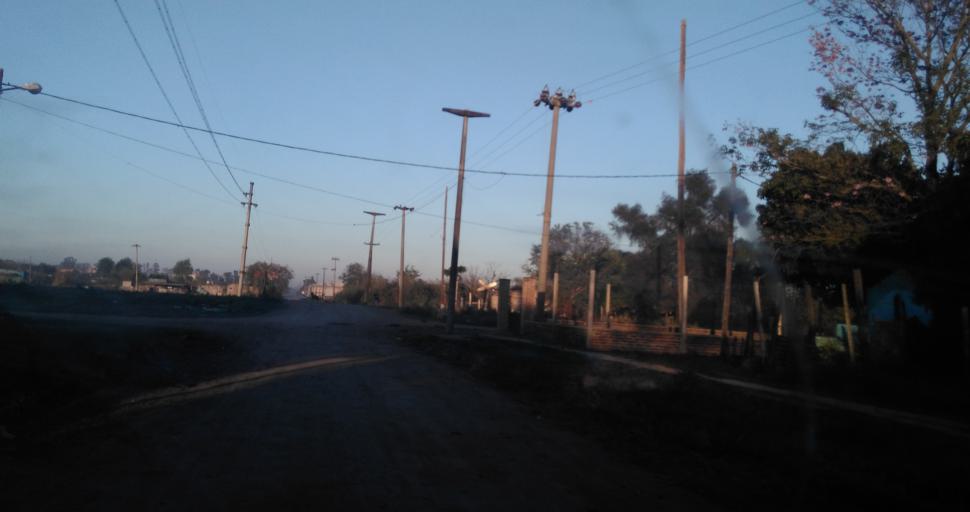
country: AR
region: Chaco
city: Fontana
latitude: -27.4284
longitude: -59.0203
